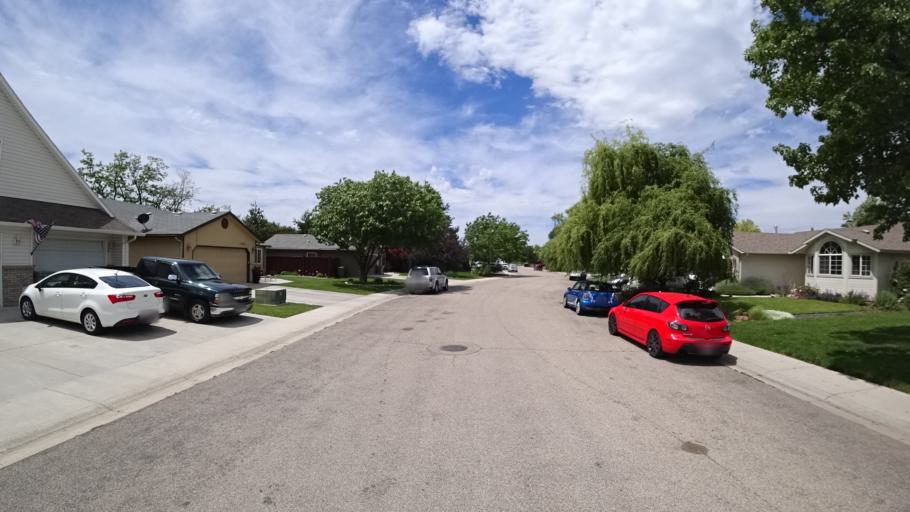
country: US
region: Idaho
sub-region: Ada County
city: Meridian
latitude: 43.6290
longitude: -116.3224
